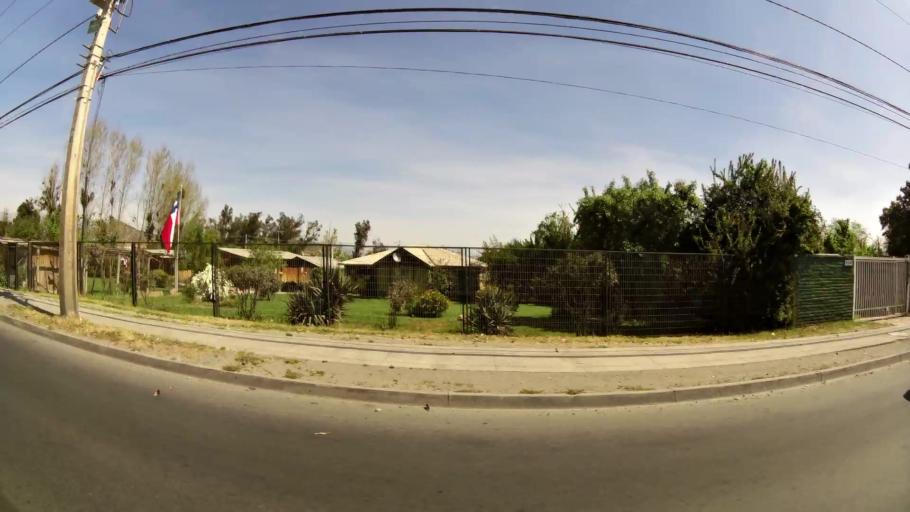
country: CL
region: Santiago Metropolitan
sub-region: Provincia de Cordillera
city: Puente Alto
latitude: -33.5840
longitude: -70.5466
